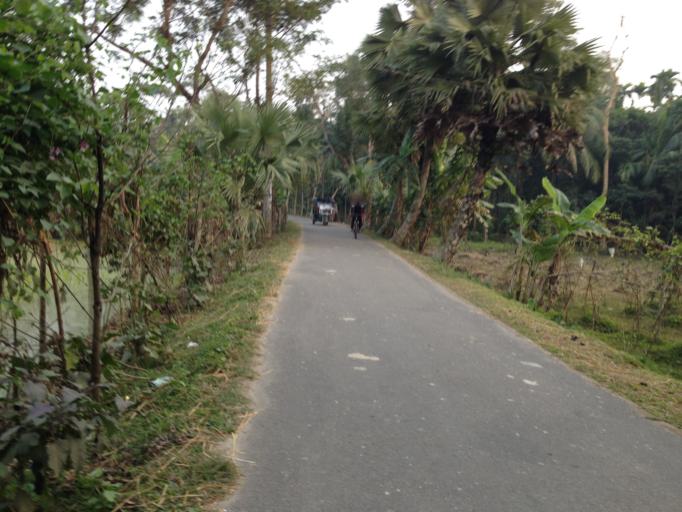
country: BD
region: Chittagong
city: Lakshmipur
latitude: 22.9191
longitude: 90.8410
